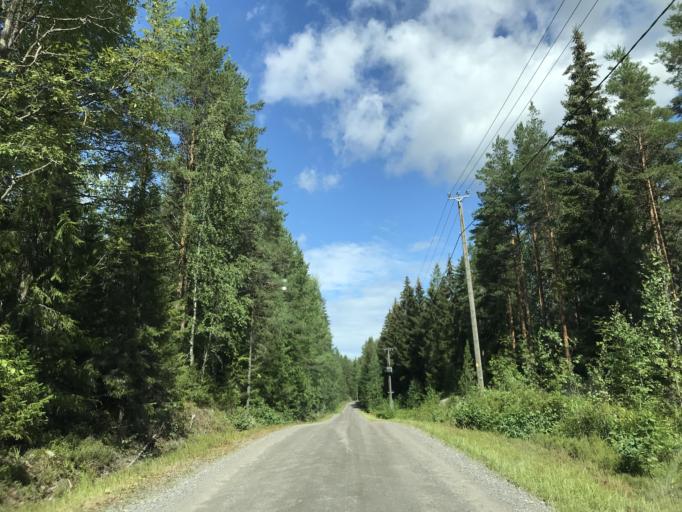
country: FI
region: Uusimaa
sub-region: Helsinki
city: Kaerkoelae
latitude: 60.6291
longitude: 23.7740
